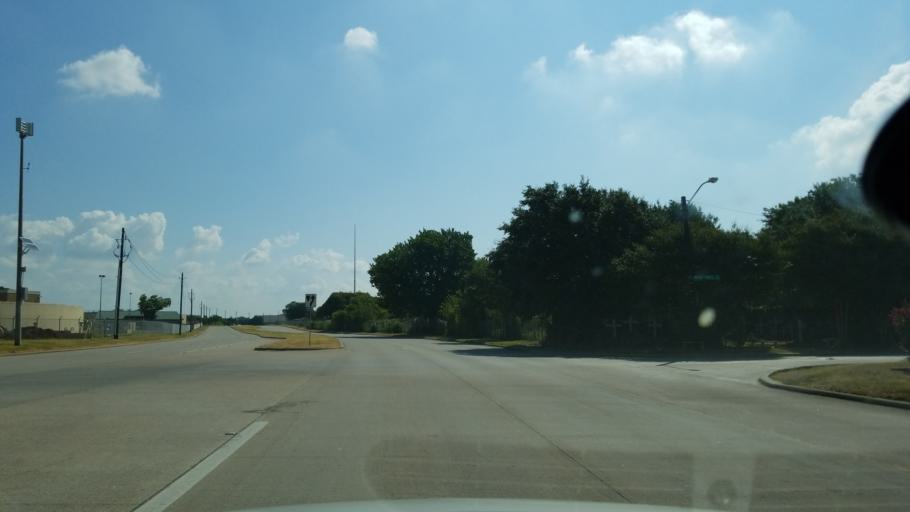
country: US
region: Texas
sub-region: Tarrant County
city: Bedford
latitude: 32.8082
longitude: -97.1296
